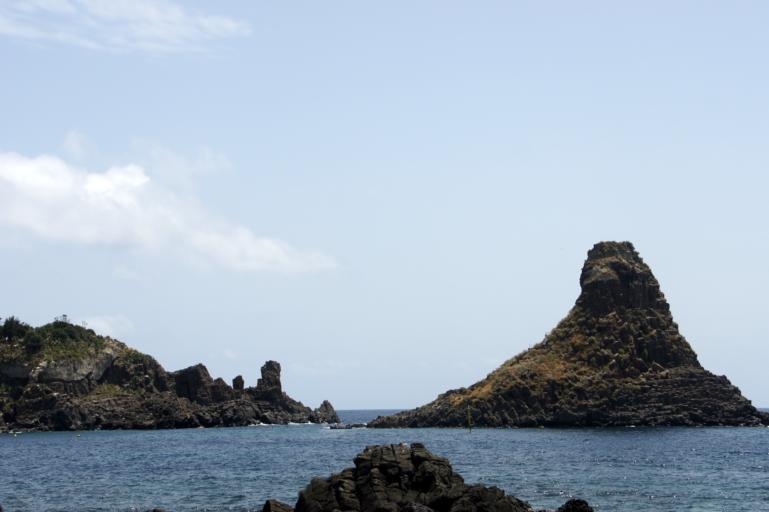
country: IT
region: Sicily
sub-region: Catania
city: Acitrezza
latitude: 37.5596
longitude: 15.1601
